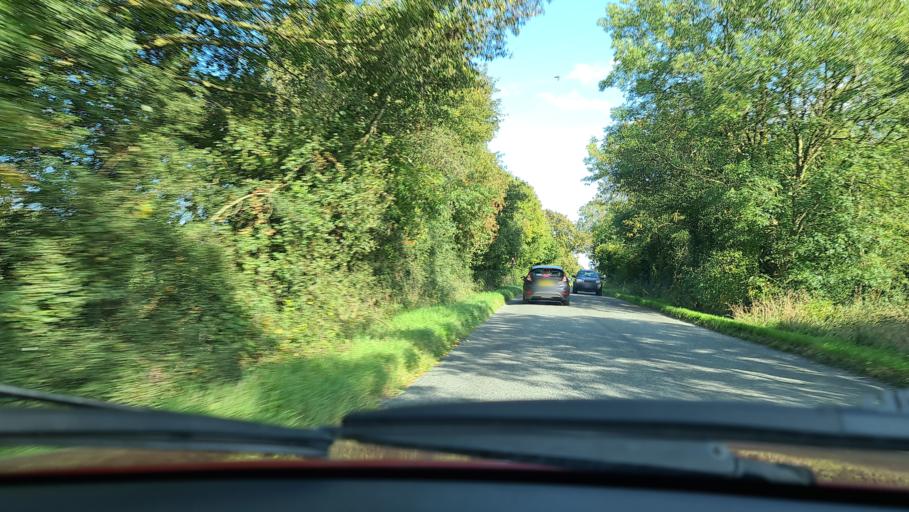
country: GB
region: England
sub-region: Northamptonshire
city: Brackley
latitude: 52.0170
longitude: -1.1918
